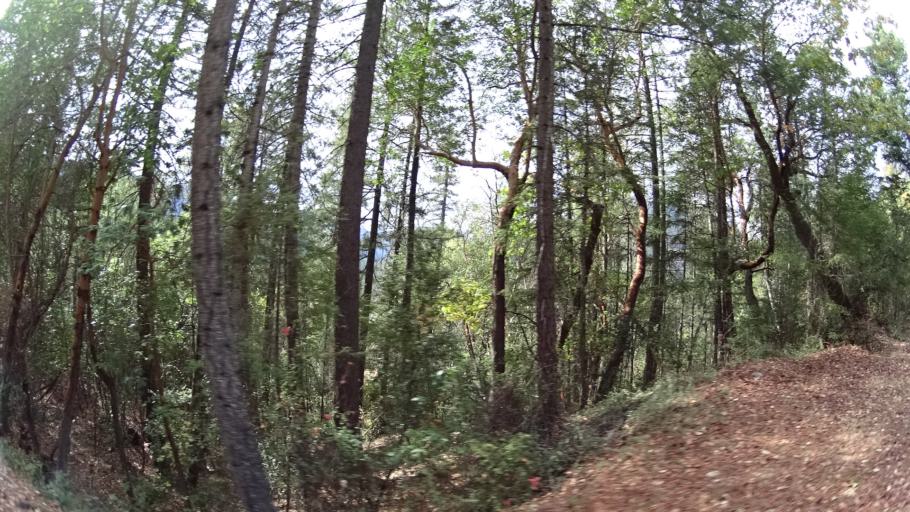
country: US
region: California
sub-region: Siskiyou County
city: Happy Camp
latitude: 41.7915
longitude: -123.3074
